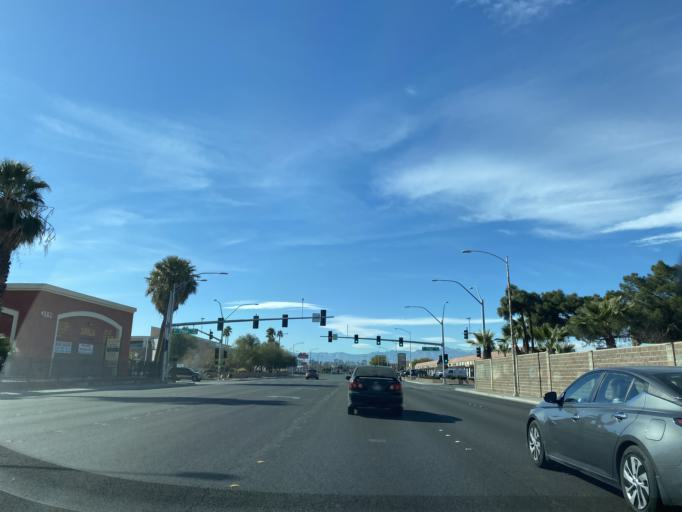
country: US
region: Nevada
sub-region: Clark County
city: Sunrise Manor
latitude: 36.1737
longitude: -115.0751
